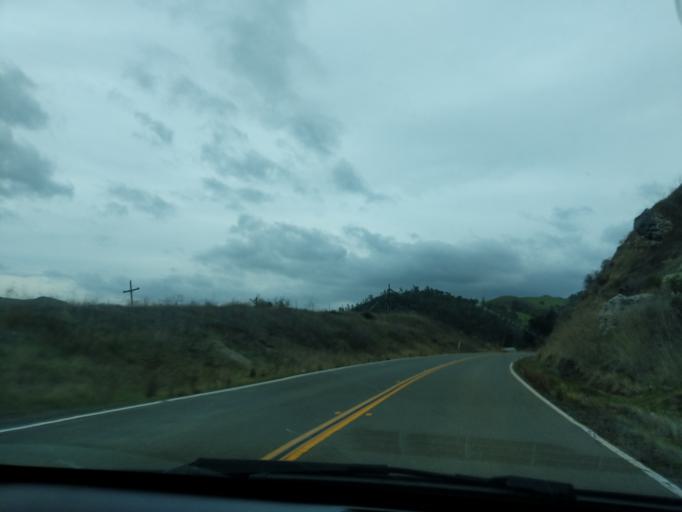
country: US
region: California
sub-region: Monterey County
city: Soledad
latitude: 36.6006
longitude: -121.1947
